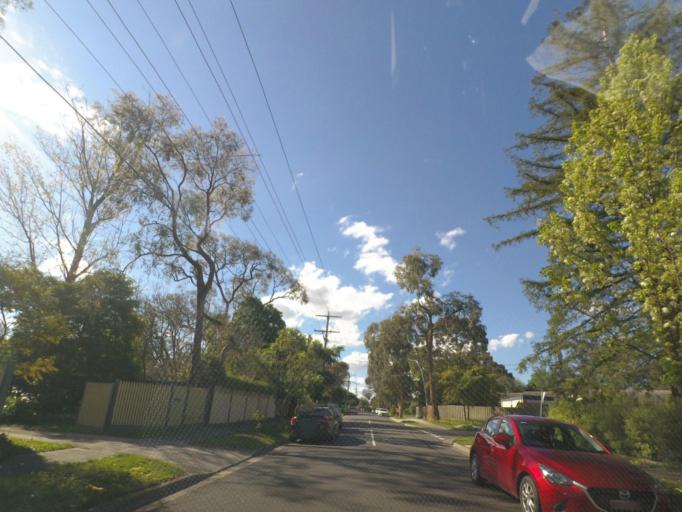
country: AU
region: Victoria
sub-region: Knox
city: Knoxfield
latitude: -37.8880
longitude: 145.2491
